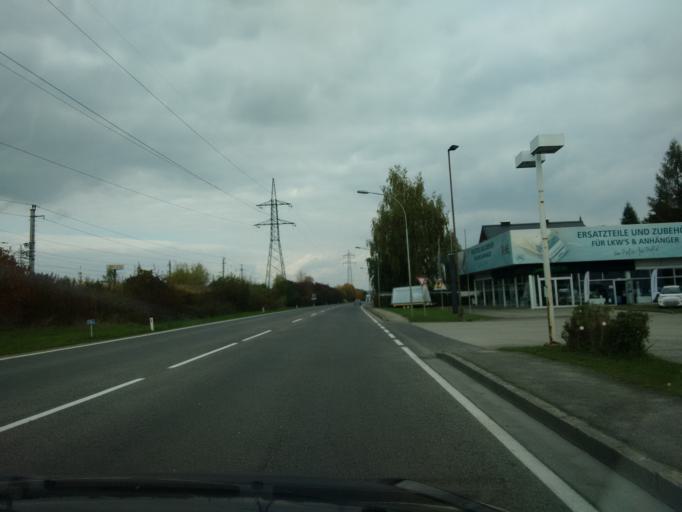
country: AT
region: Upper Austria
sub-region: Politischer Bezirk Vocklabruck
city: Redlham
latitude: 48.0204
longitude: 13.7289
